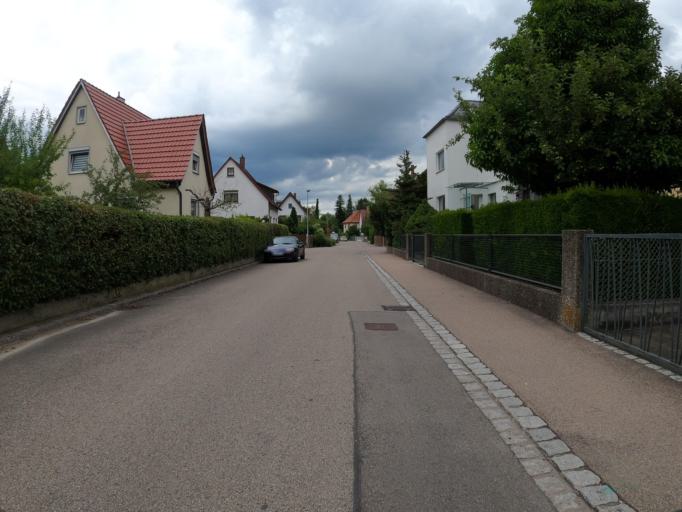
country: DE
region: Baden-Wuerttemberg
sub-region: Tuebingen Region
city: Langenau
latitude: 48.4975
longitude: 10.1270
